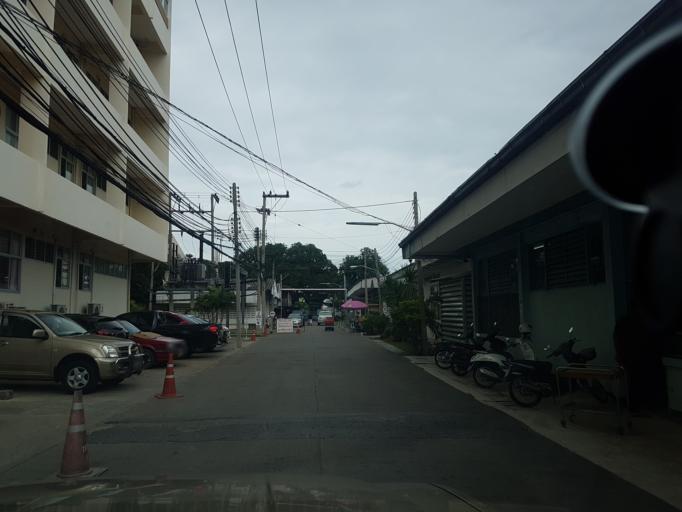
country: TH
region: Lop Buri
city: Lop Buri
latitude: 14.8043
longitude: 100.6534
